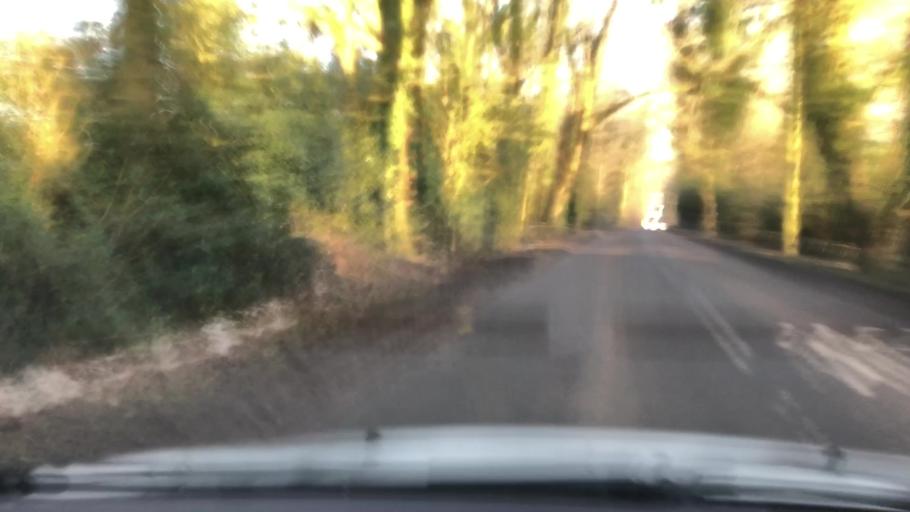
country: GB
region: England
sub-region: Hampshire
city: Alton
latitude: 51.1878
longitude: -1.0026
